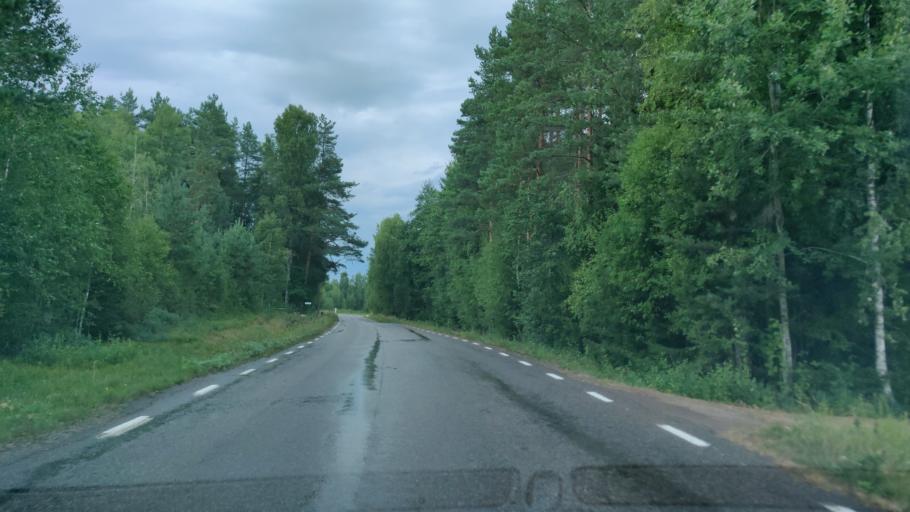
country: SE
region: Vaermland
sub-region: Munkfors Kommun
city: Munkfors
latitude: 59.8790
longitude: 13.5222
